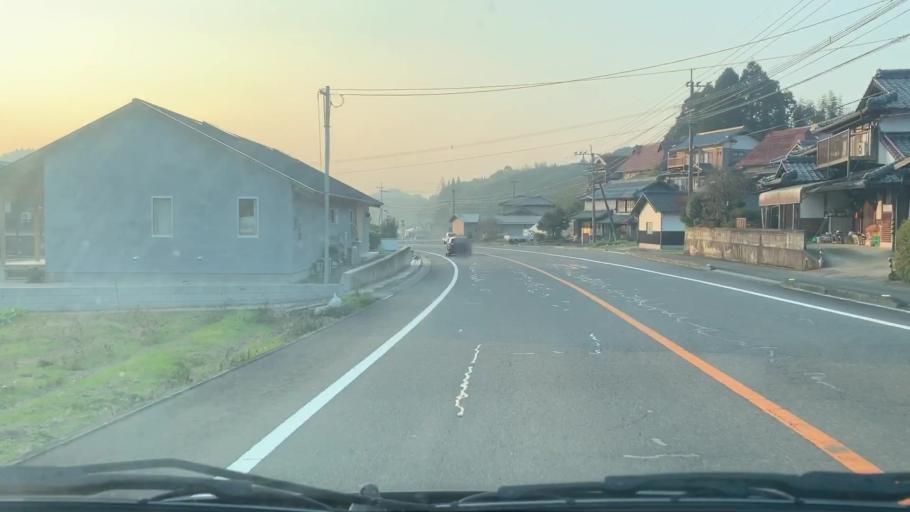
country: JP
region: Saga Prefecture
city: Takeocho-takeo
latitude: 33.2560
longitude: 130.0102
